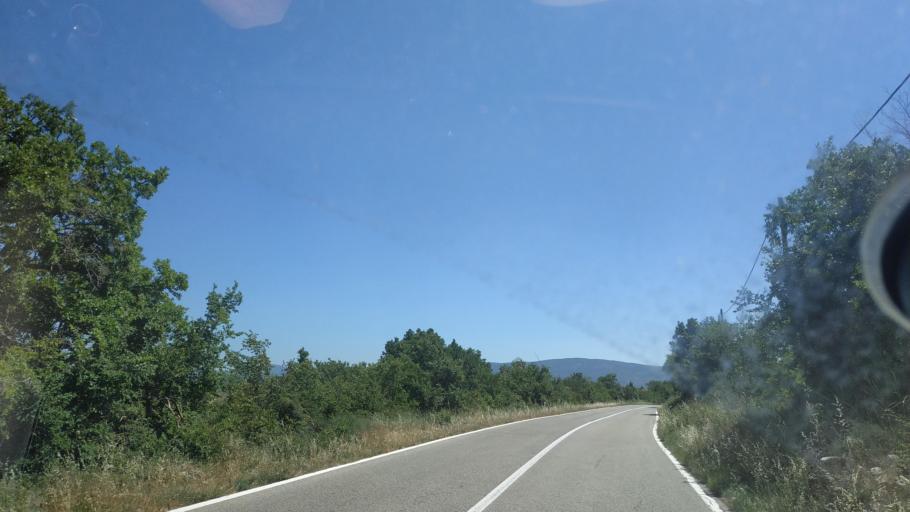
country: HR
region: Sibensko-Kniniska
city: Drnis
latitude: 43.8962
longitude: 16.2104
